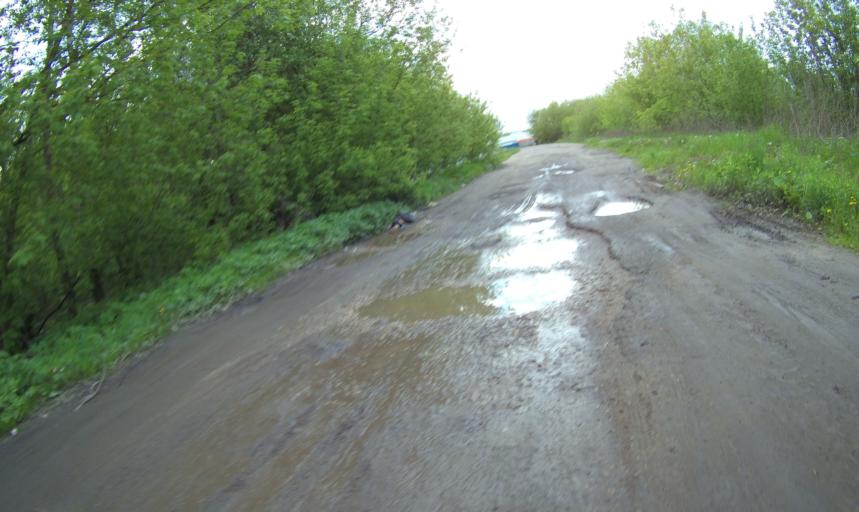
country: RU
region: Moskovskaya
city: Ramenskoye
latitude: 55.5647
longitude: 38.2767
